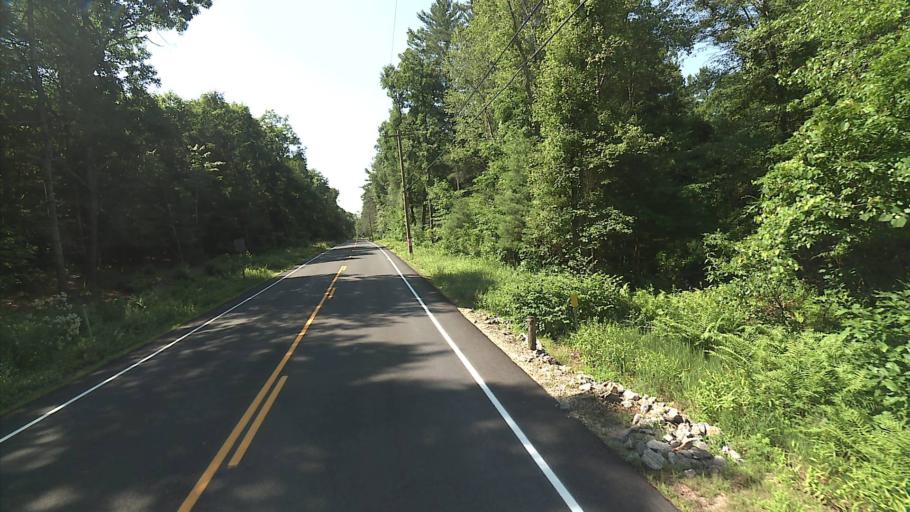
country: US
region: Connecticut
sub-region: Litchfield County
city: Terryville
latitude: 41.7217
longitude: -73.0138
